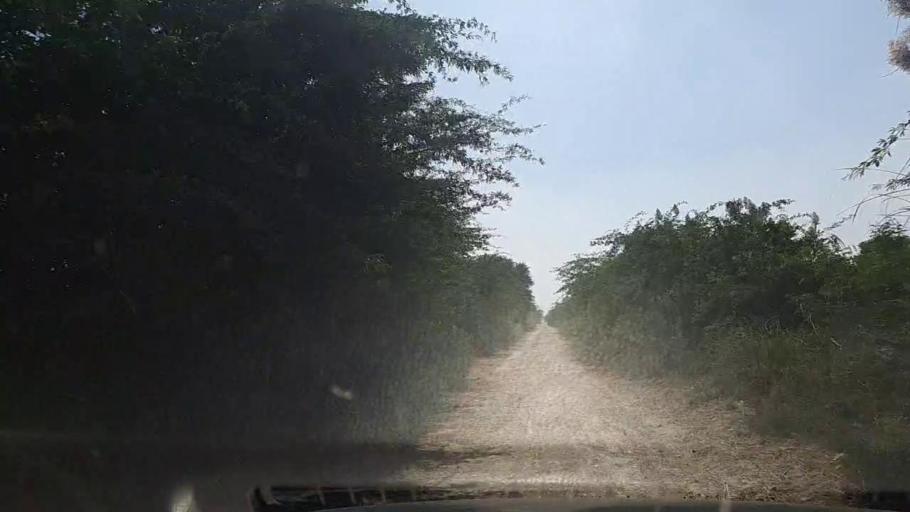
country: PK
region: Sindh
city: Daro Mehar
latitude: 24.8347
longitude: 68.0917
